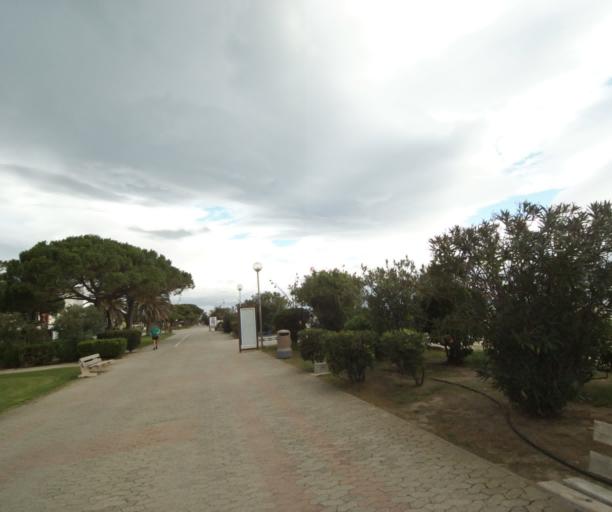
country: FR
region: Languedoc-Roussillon
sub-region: Departement des Pyrenees-Orientales
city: Argelers
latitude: 42.5503
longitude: 3.0485
